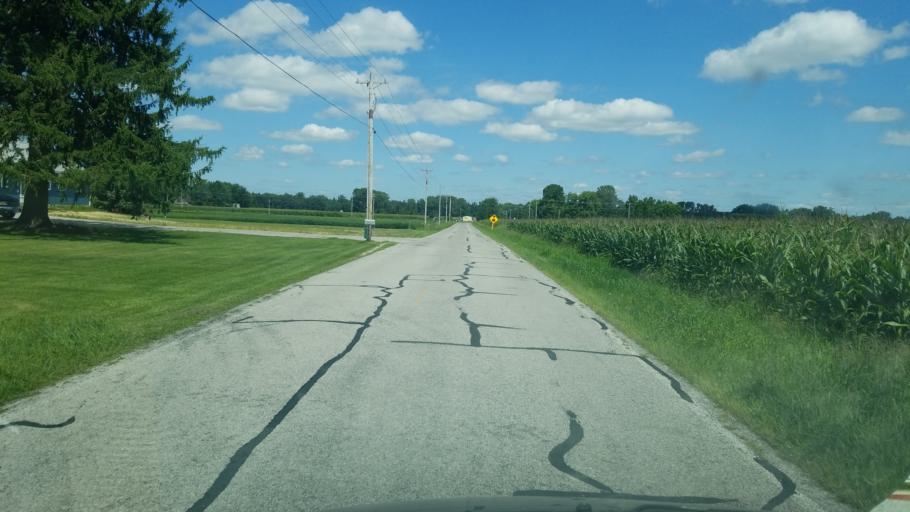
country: US
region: Ohio
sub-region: Fulton County
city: Delta
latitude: 41.5123
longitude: -83.9414
